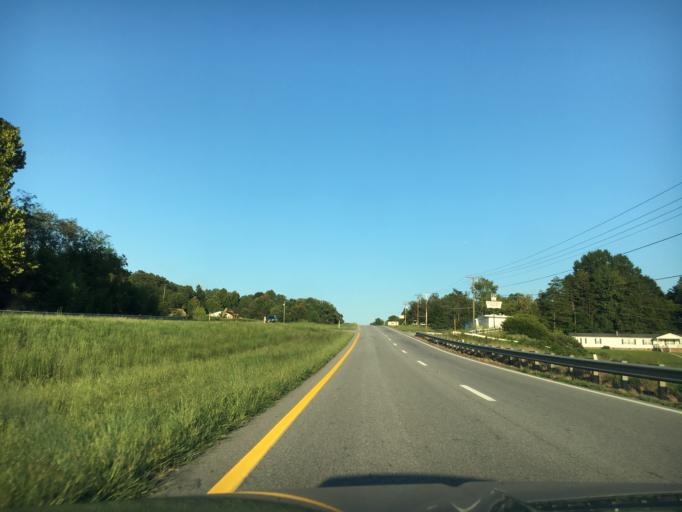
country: US
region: Virginia
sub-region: City of Danville
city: Danville
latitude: 36.5807
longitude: -79.2888
